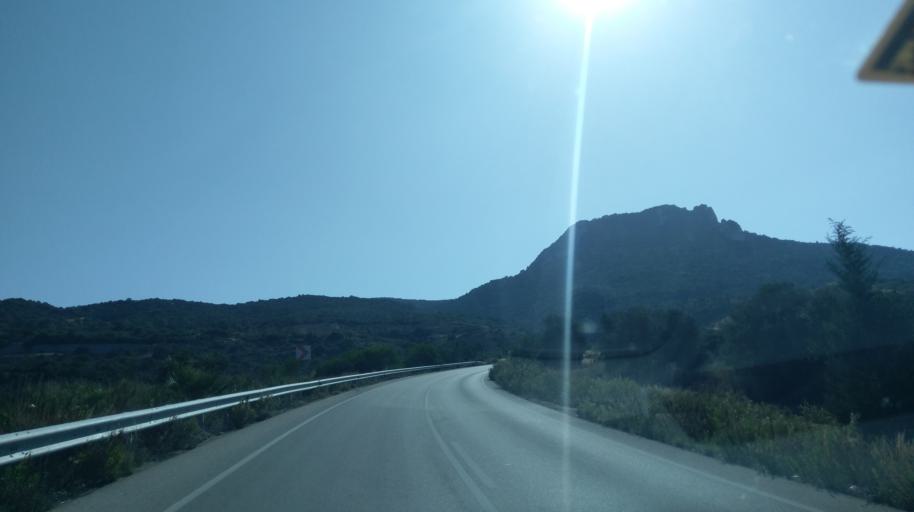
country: CY
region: Ammochostos
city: Trikomo
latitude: 35.4343
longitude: 33.9620
